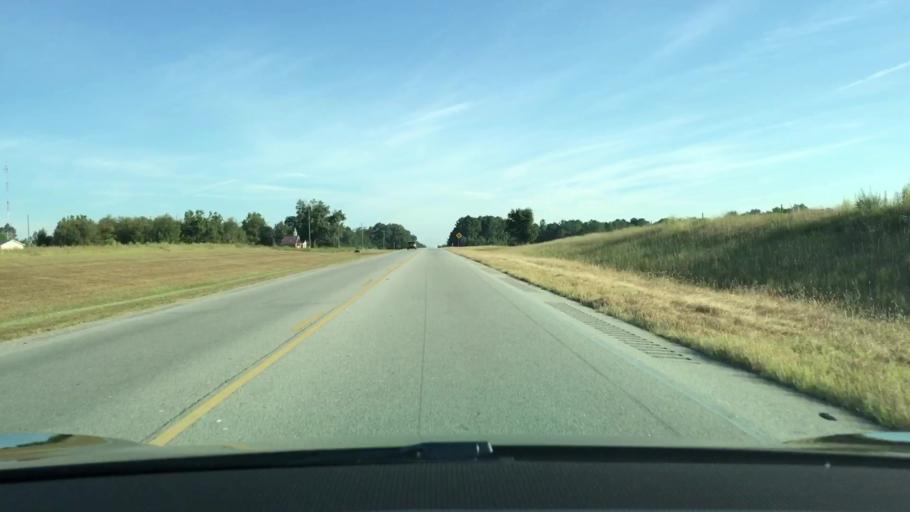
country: US
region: Georgia
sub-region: Jefferson County
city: Louisville
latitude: 32.9455
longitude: -82.3949
